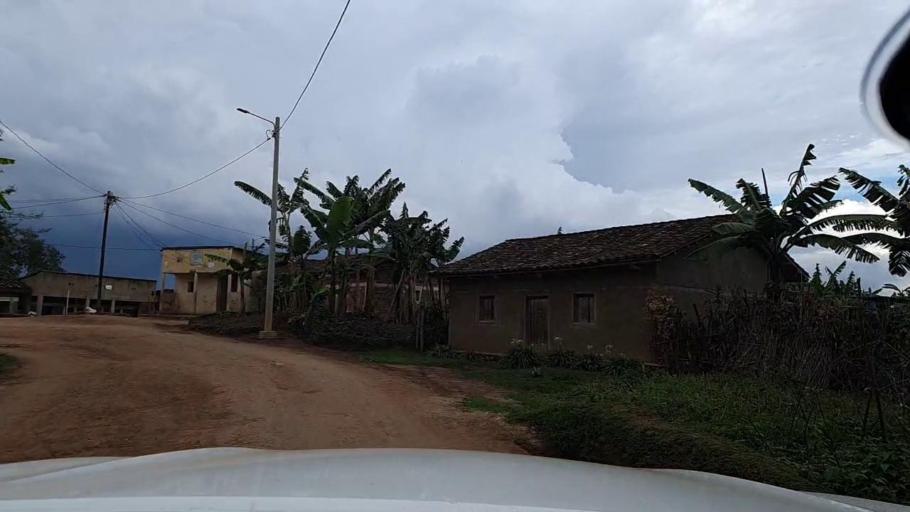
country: BI
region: Kayanza
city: Kayanza
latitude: -2.7995
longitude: 29.5064
